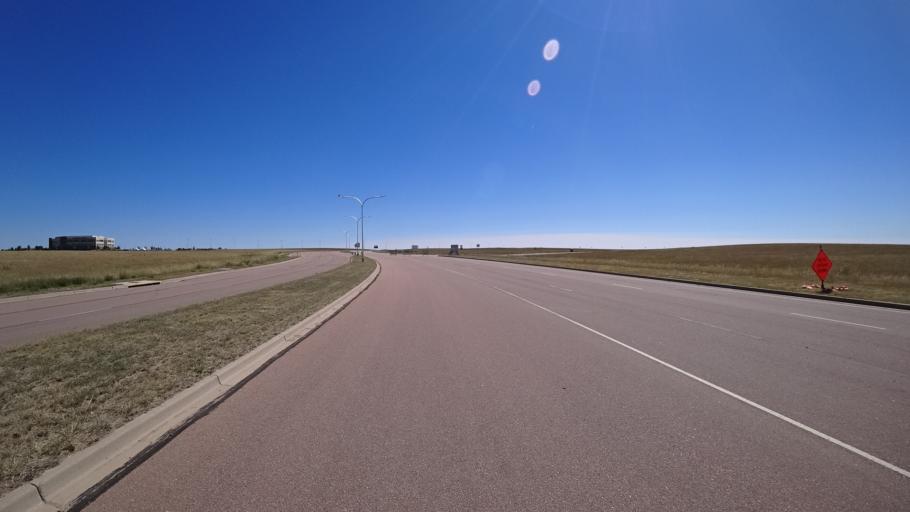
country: US
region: Colorado
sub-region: El Paso County
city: Security-Widefield
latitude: 38.7773
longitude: -104.7082
